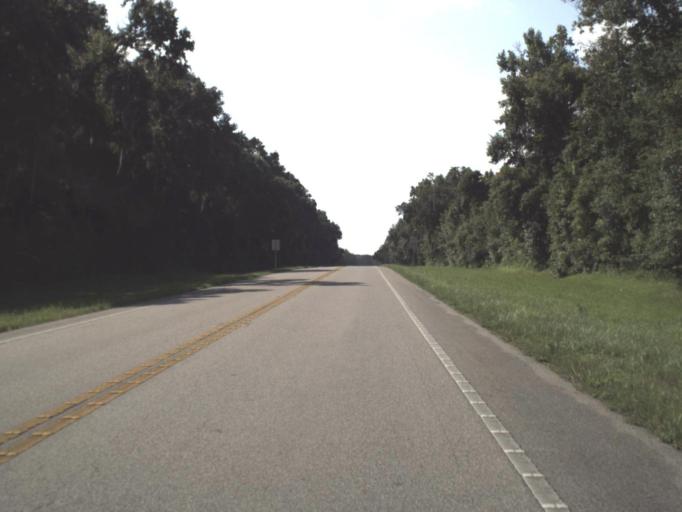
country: US
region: Florida
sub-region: Hernando County
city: North Brooksville
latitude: 28.6230
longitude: -82.4170
